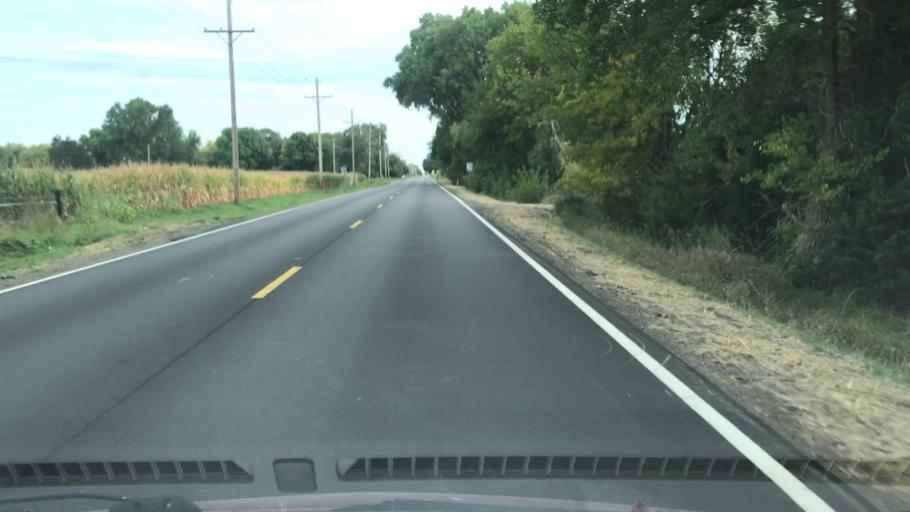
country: US
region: Nebraska
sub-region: Hall County
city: Grand Island
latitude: 40.9258
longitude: -98.3015
